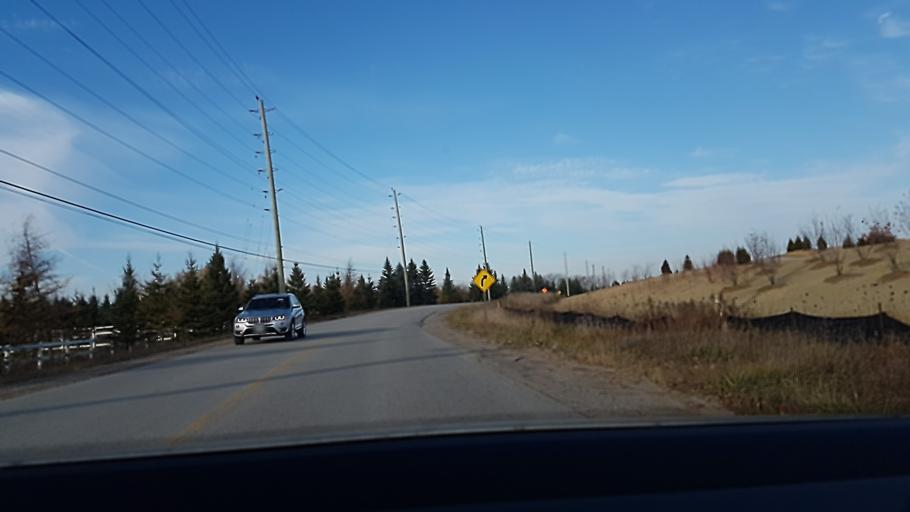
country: CA
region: Ontario
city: Barrie
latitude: 44.3842
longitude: -79.5552
